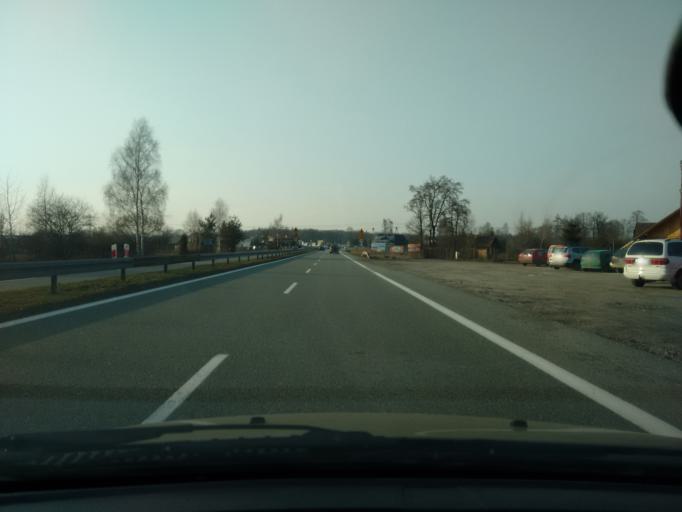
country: PL
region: Silesian Voivodeship
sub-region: Powiat cieszynski
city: Zbytkow
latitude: 49.9010
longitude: 18.7397
